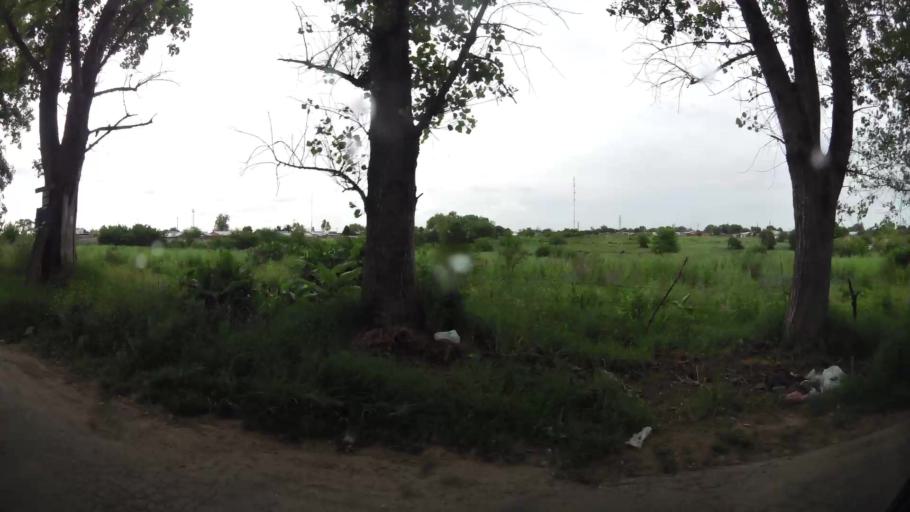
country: AR
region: Buenos Aires
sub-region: Partido de Zarate
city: Zarate
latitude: -34.1194
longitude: -59.0239
